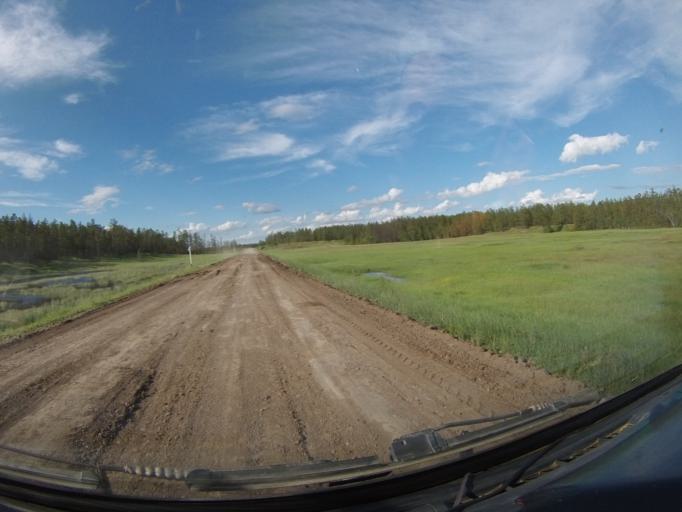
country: RU
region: Sakha
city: Ytyk-Kyuyel'
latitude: 62.2256
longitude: 133.2858
